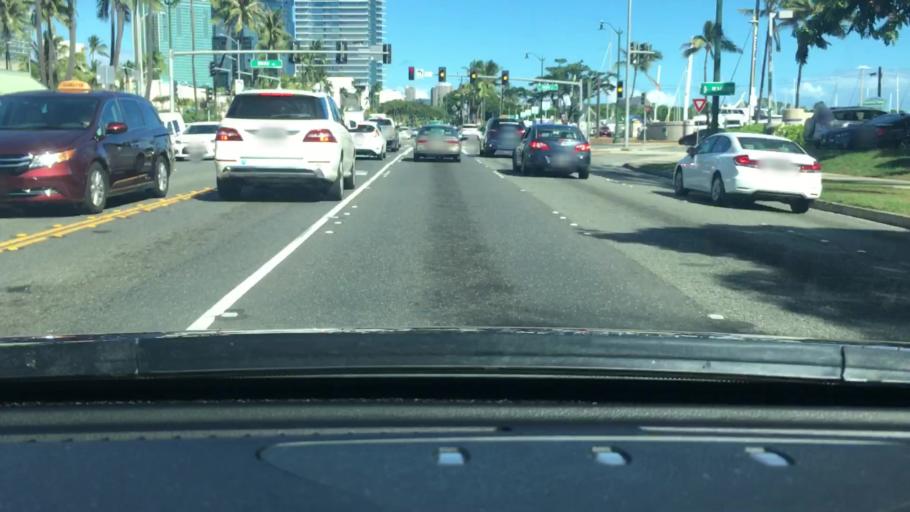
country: US
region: Hawaii
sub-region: Honolulu County
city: Honolulu
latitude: 21.2953
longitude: -157.8585
